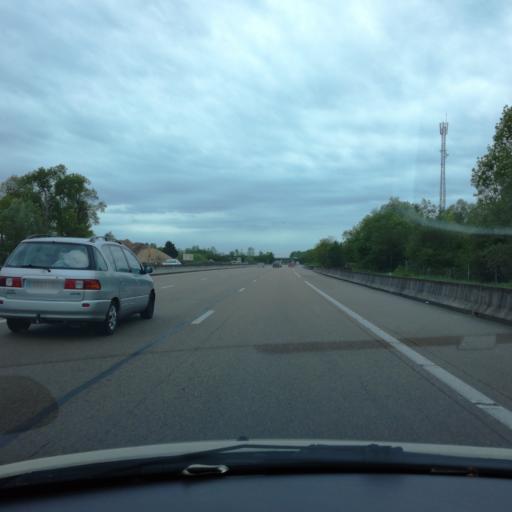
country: FR
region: Bourgogne
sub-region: Departement de la Cote-d'Or
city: Arc-sur-Tille
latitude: 47.3670
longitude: 5.1644
